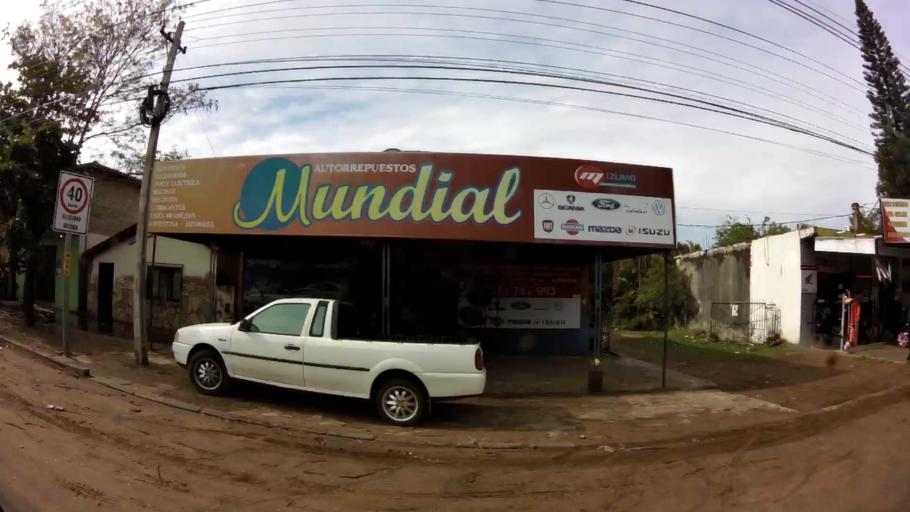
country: PY
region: Central
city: Limpio
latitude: -25.1690
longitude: -57.4767
